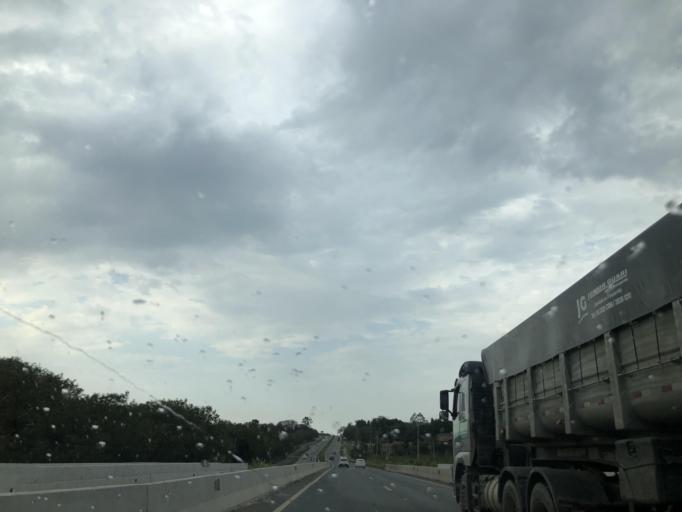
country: BR
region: Sao Paulo
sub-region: Salto De Pirapora
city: Salto de Pirapora
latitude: -23.6372
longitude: -47.5725
